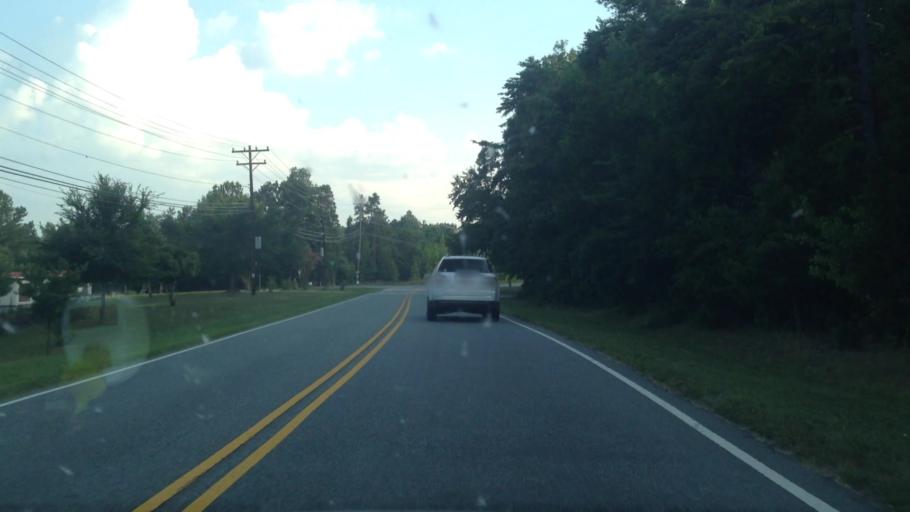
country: US
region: North Carolina
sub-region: Davidson County
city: Wallburg
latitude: 35.9708
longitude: -80.0849
